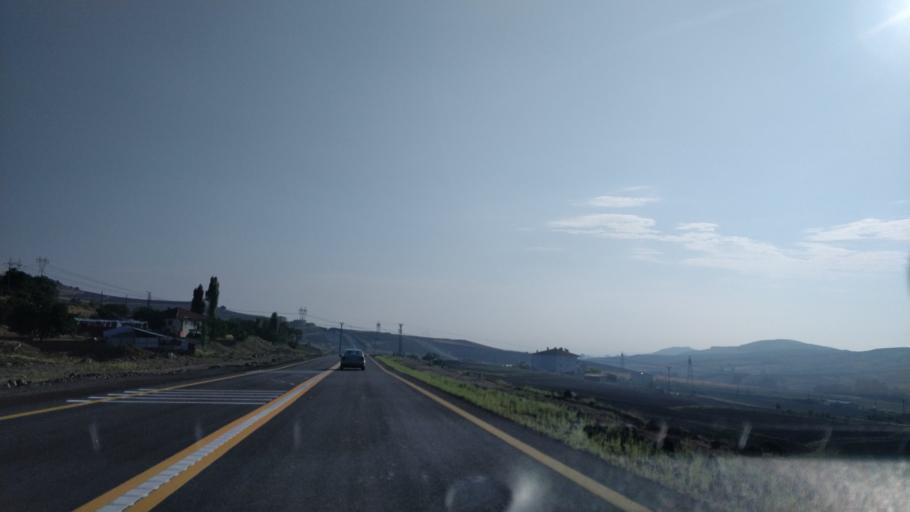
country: TR
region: Ankara
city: Etimesgut
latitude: 39.8610
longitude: 32.5816
